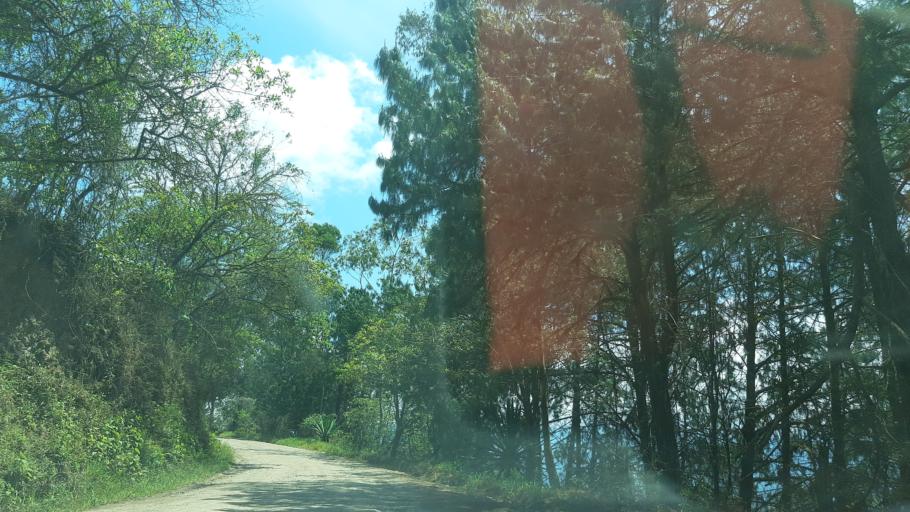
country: CO
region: Boyaca
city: Chinavita
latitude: 5.1245
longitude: -73.3855
